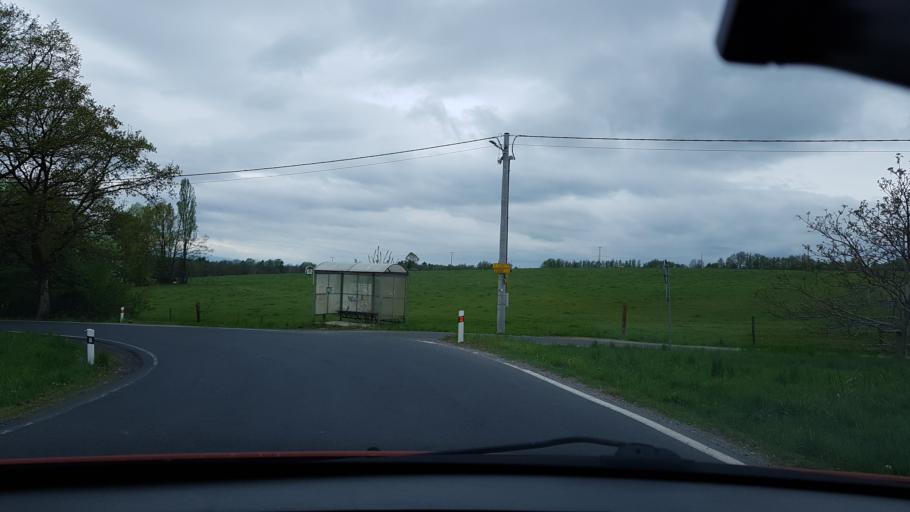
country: CZ
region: Olomoucky
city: Mikulovice
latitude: 50.3134
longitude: 17.2990
